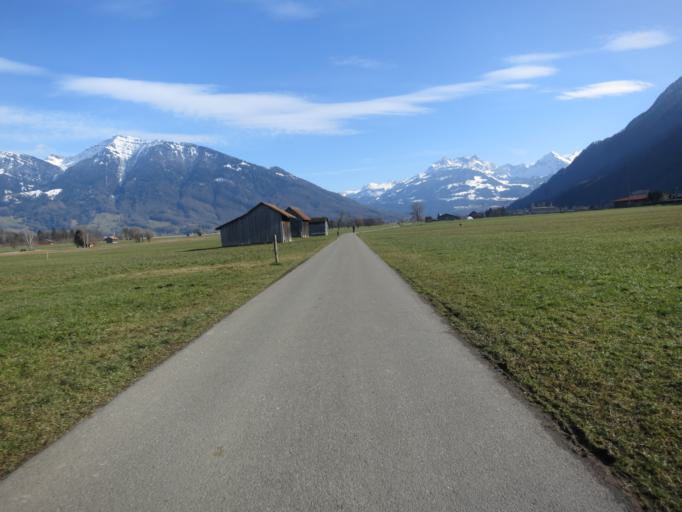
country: CH
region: Schwyz
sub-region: Bezirk March
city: Reichenburg
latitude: 47.1718
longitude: 8.9924
